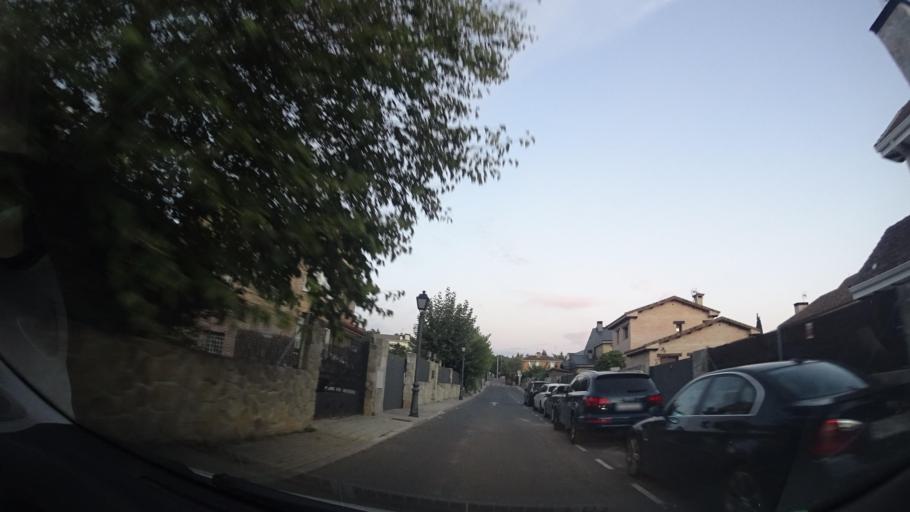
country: ES
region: Madrid
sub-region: Provincia de Madrid
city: Colmenarejo
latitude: 40.5652
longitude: -4.0156
